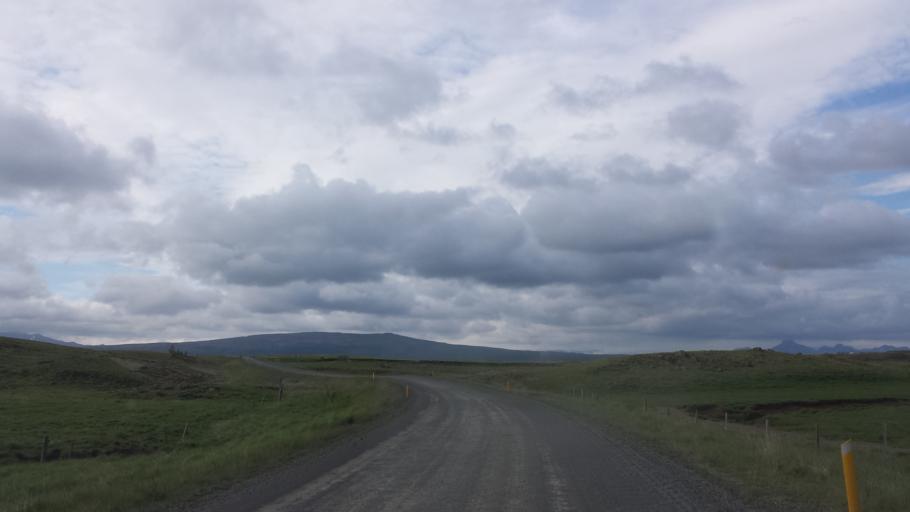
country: IS
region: South
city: Vestmannaeyjar
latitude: 64.2856
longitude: -20.2250
